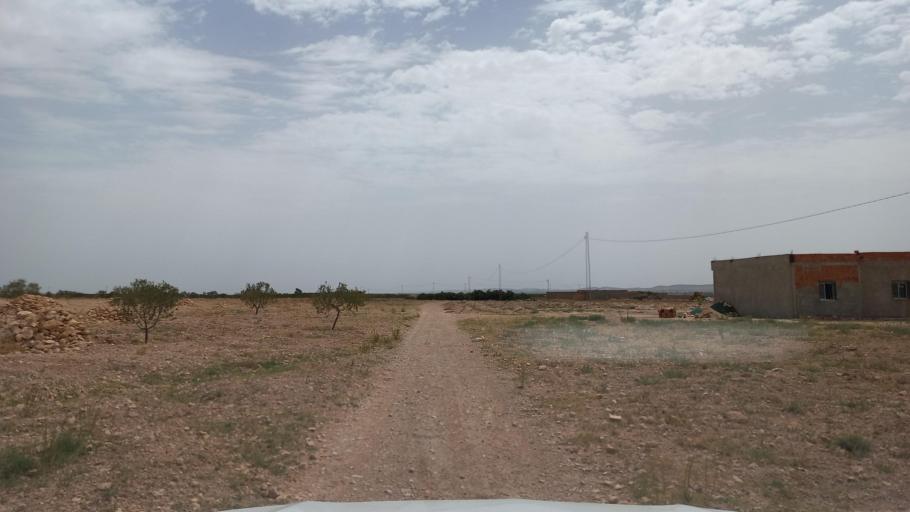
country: TN
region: Al Qasrayn
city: Kasserine
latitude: 35.2909
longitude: 9.0025
